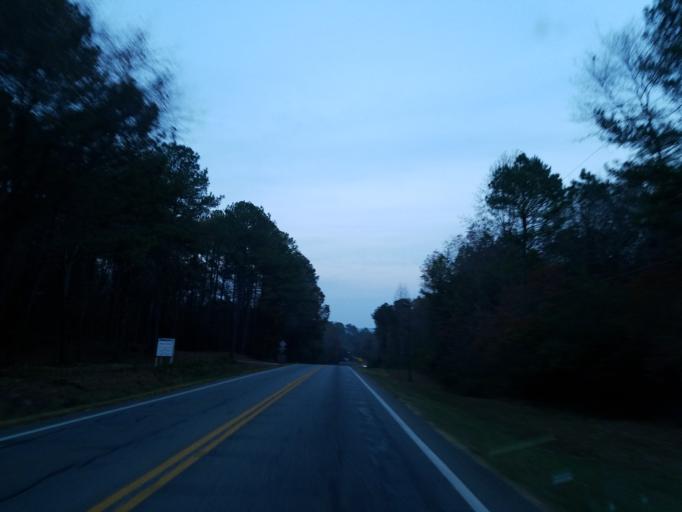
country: US
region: Georgia
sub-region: Pickens County
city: Jasper
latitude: 34.5118
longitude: -84.5456
